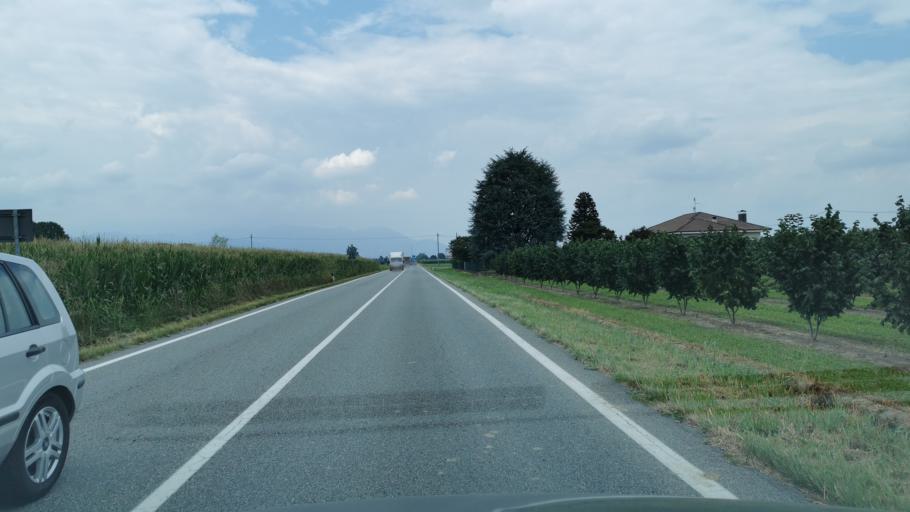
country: IT
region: Piedmont
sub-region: Provincia di Torino
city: Cavour
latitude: 44.8094
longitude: 7.3723
